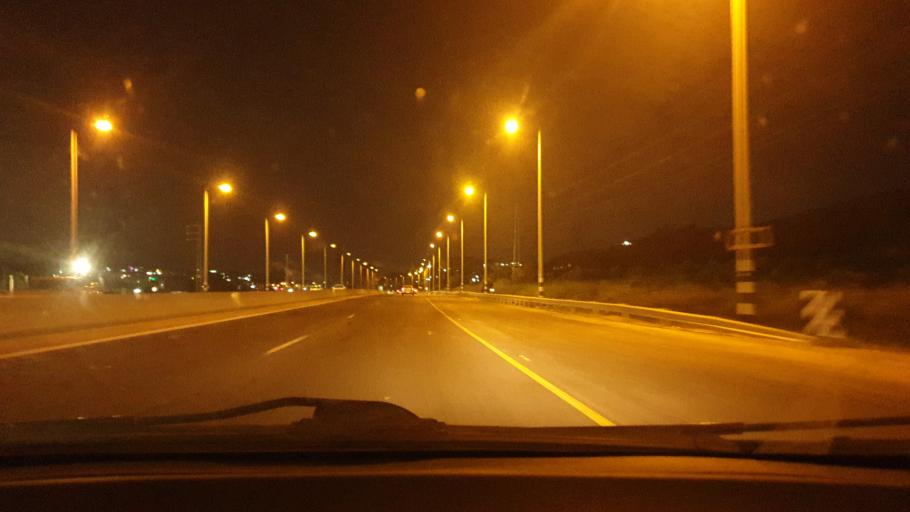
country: PS
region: West Bank
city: Barta`ah ash Sharqiyah
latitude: 32.5061
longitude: 35.0956
